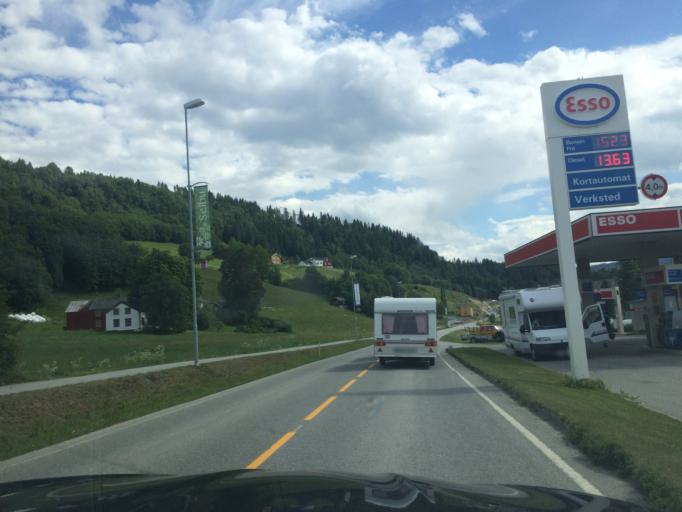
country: NO
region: Sor-Trondelag
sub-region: Selbu
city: Mebonden
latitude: 63.2184
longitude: 11.0425
